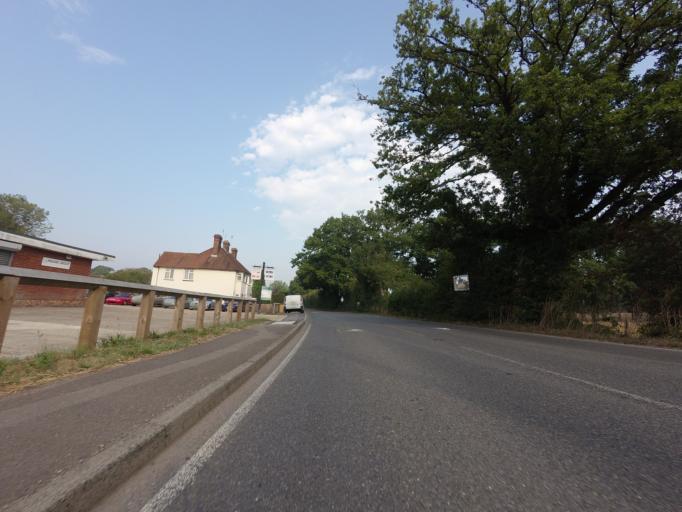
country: GB
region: England
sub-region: Kent
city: Tenterden
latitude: 51.1256
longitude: 0.7614
